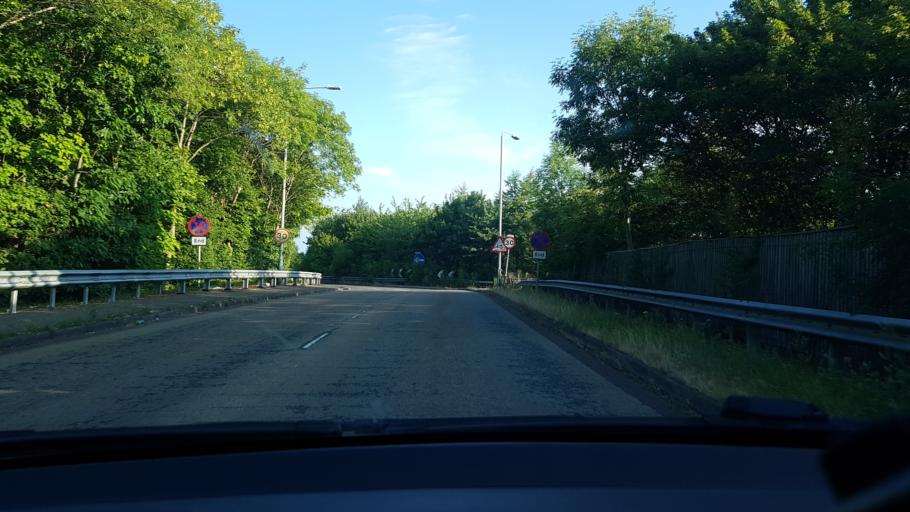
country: GB
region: England
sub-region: Nottinghamshire
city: Eastwood
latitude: 53.0170
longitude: -1.3198
